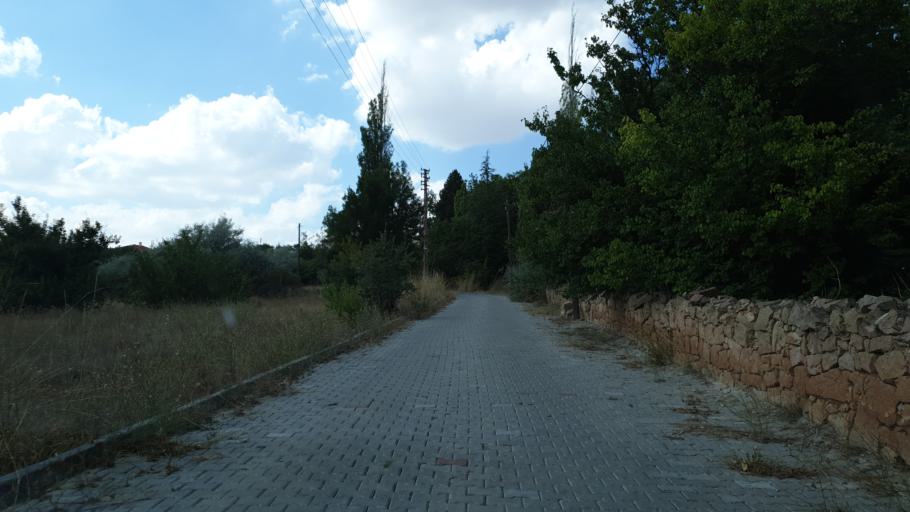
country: TR
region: Kayseri
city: Felahiye
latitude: 39.1150
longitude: 35.6095
